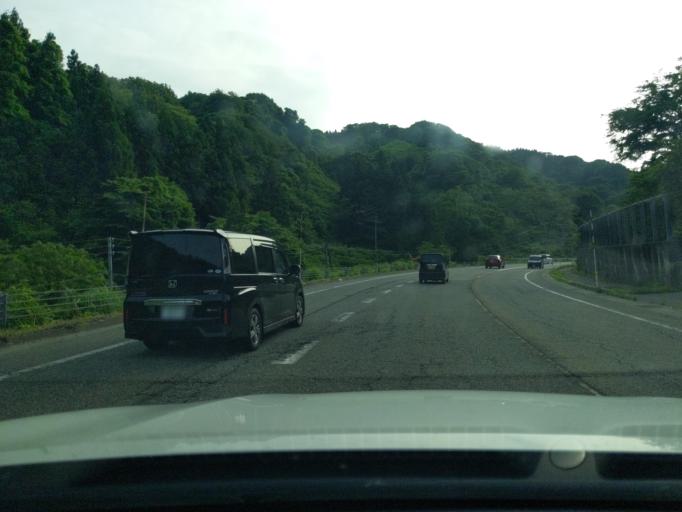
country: JP
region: Niigata
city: Kashiwazaki
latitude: 37.4095
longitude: 138.6716
